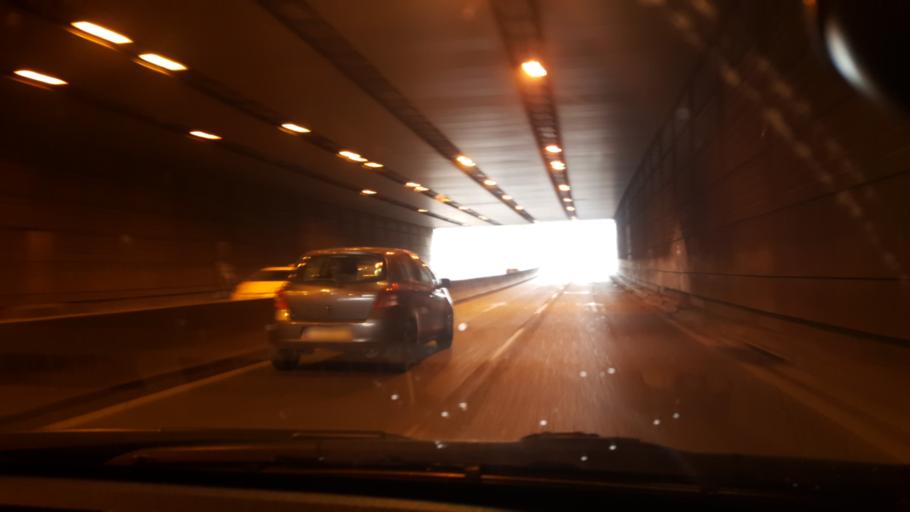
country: GR
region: Attica
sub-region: Nomarchia Athinas
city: Neo Psychiko
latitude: 38.0046
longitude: 23.7755
